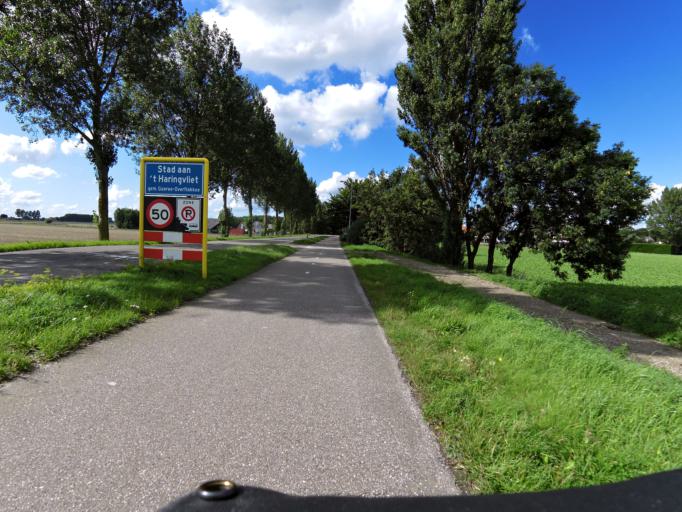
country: NL
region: South Holland
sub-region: Gemeente Goeree-Overflakkee
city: Middelharnis
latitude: 51.7297
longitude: 4.2387
